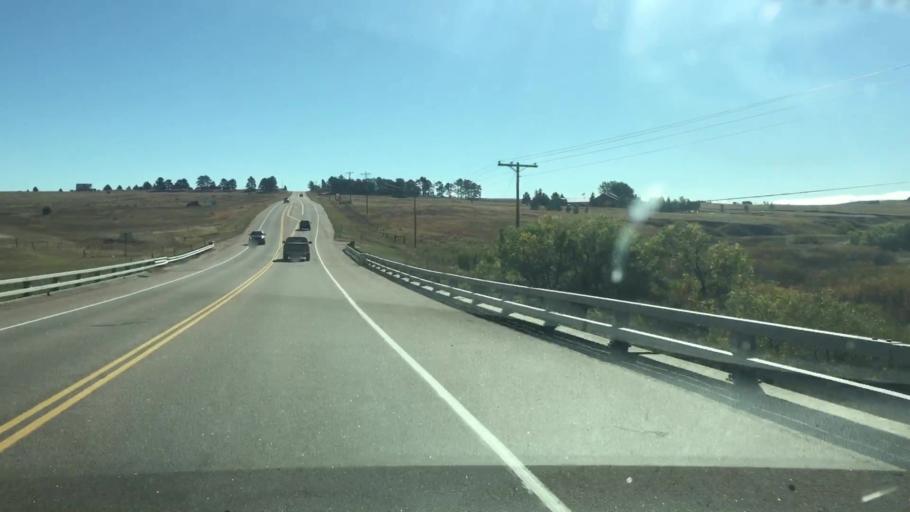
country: US
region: Colorado
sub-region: Elbert County
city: Elizabeth
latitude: 39.3590
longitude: -104.5356
